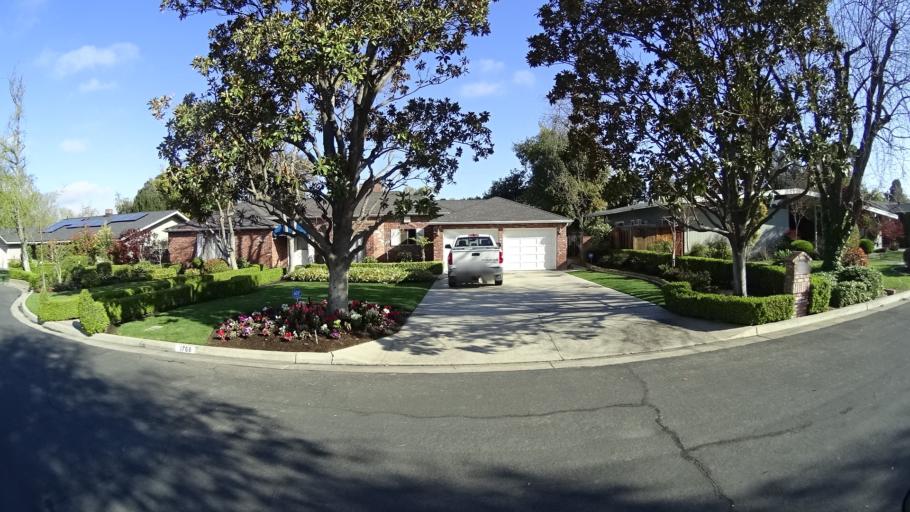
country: US
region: California
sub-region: Fresno County
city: Fresno
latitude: 36.8199
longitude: -119.8257
